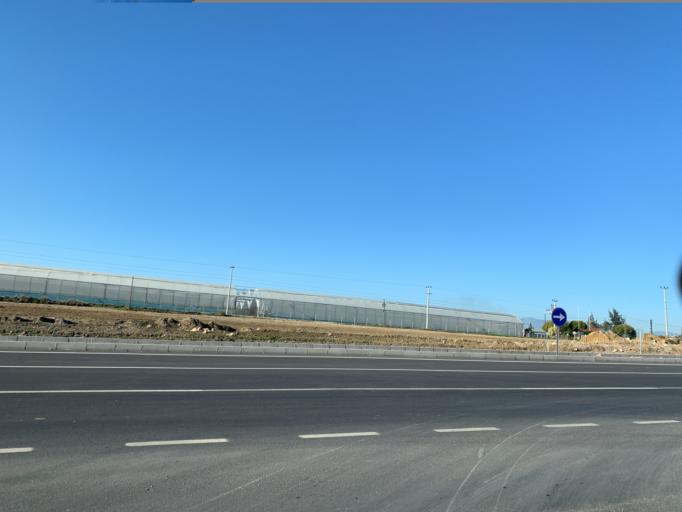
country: TR
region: Antalya
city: Aksu
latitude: 36.9608
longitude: 30.8248
